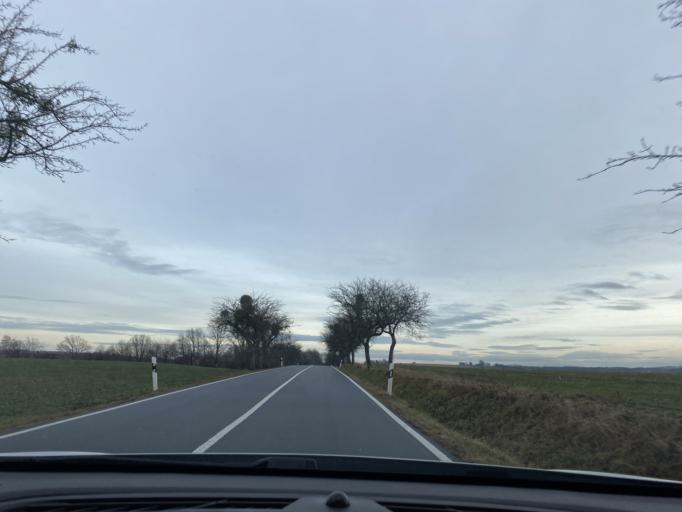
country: DE
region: Saxony
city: Reichenbach
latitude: 51.1456
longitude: 14.7860
